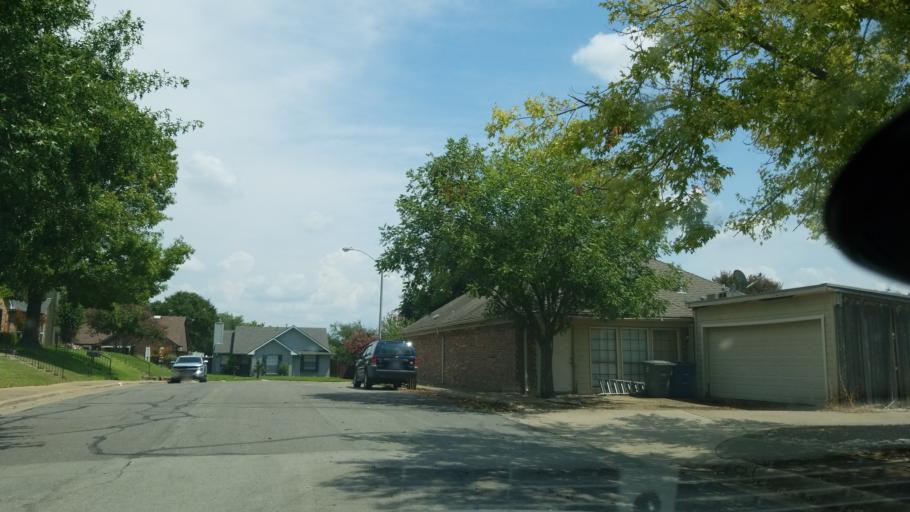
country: US
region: Texas
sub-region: Dallas County
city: Richardson
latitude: 32.8924
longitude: -96.7336
